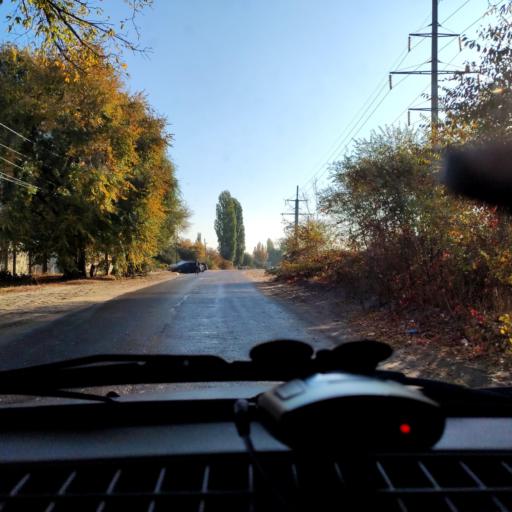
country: RU
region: Voronezj
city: Voronezh
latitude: 51.6681
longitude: 39.1453
